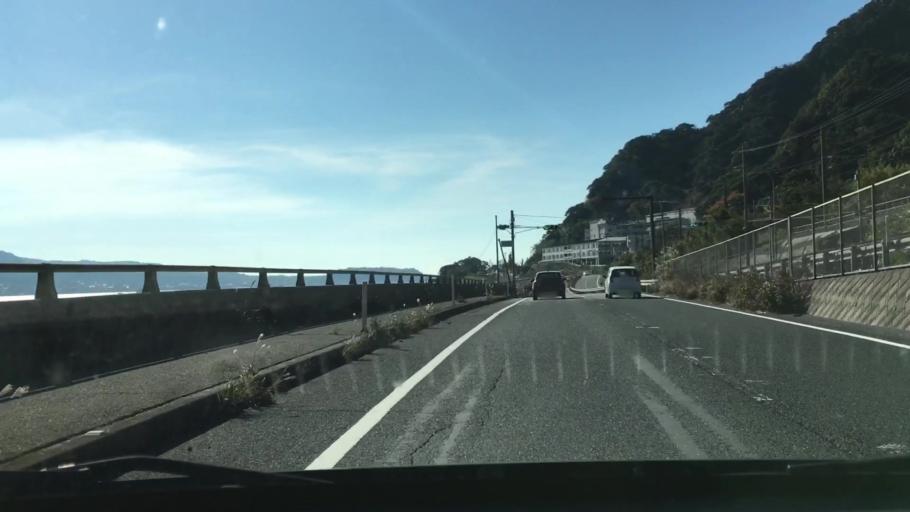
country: JP
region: Kagoshima
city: Kagoshima-shi
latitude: 31.6374
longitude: 130.6026
